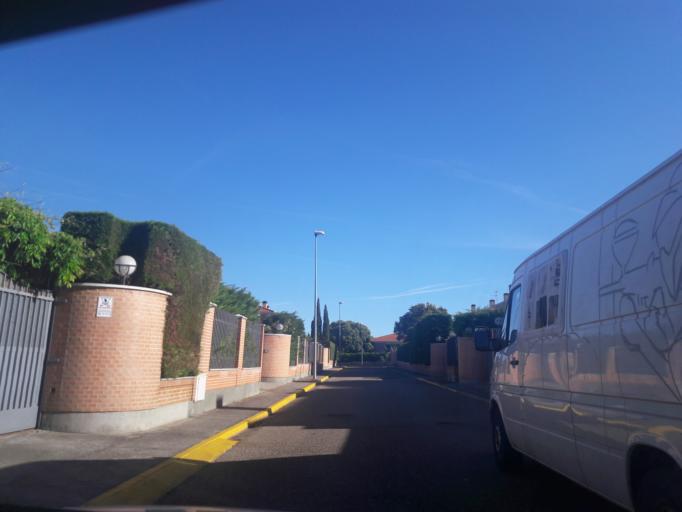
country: ES
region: Castille and Leon
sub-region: Provincia de Salamanca
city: Martinamor
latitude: 40.8061
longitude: -5.6366
